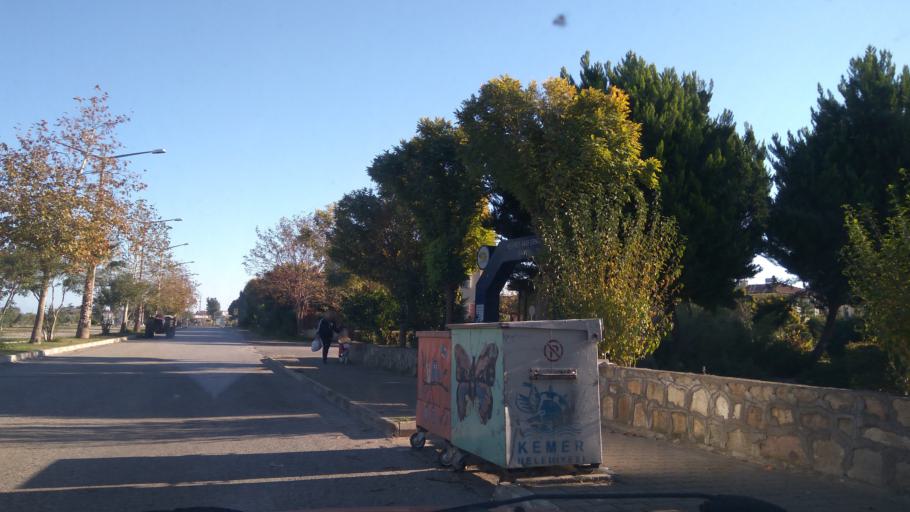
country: TR
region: Antalya
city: Kemer
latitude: 36.5693
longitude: 30.5599
